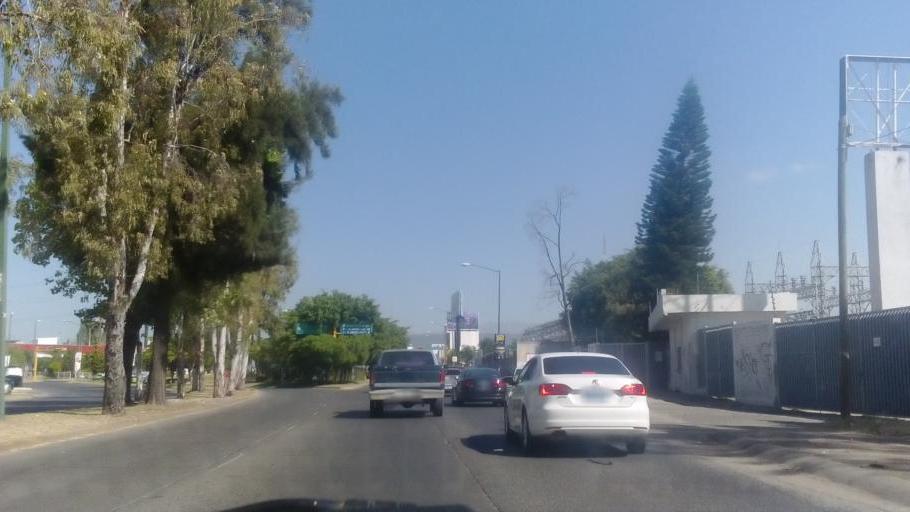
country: MX
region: Guanajuato
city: Leon
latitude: 21.1531
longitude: -101.6844
